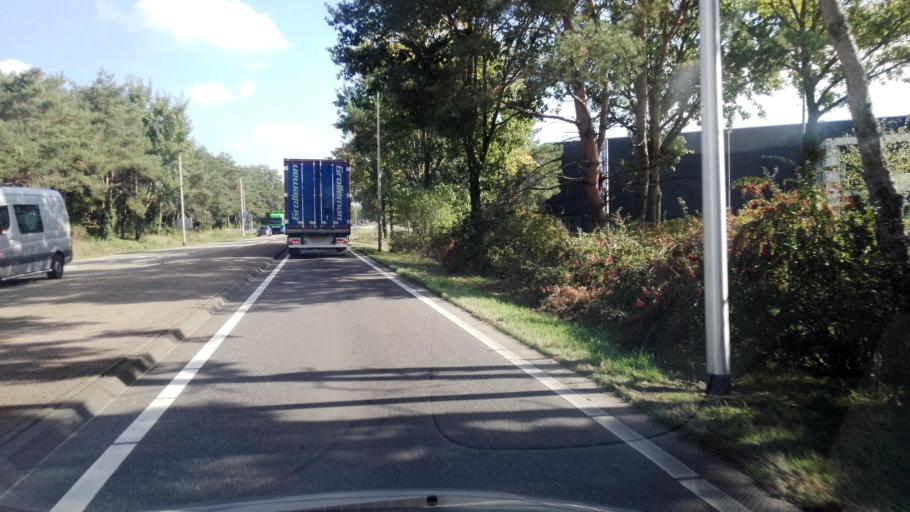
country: NL
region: North Brabant
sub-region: Gemeente Helmond
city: Helmond
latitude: 51.4519
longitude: 5.7106
